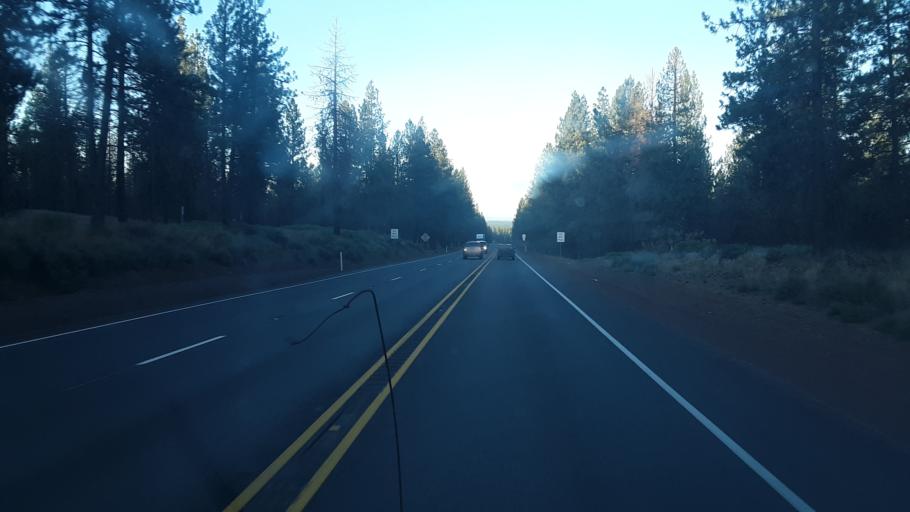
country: US
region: Oregon
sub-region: Deschutes County
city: Sunriver
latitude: 43.8611
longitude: -121.4097
